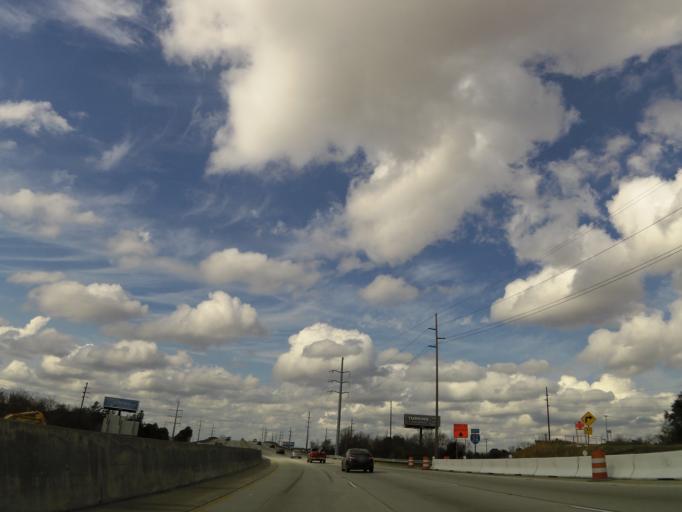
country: US
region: South Carolina
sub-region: Charleston County
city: North Charleston
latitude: 32.8324
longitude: -79.9573
